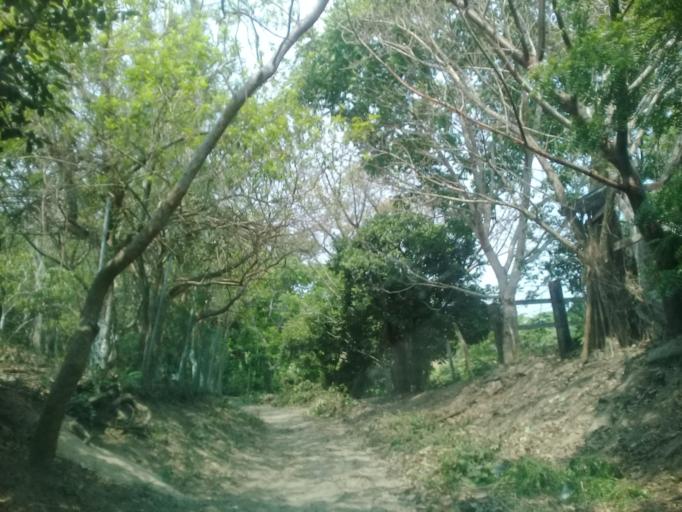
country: MX
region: Veracruz
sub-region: Veracruz
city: Fraccionamiento Geovillas los Pinos
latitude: 19.2339
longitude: -96.2418
